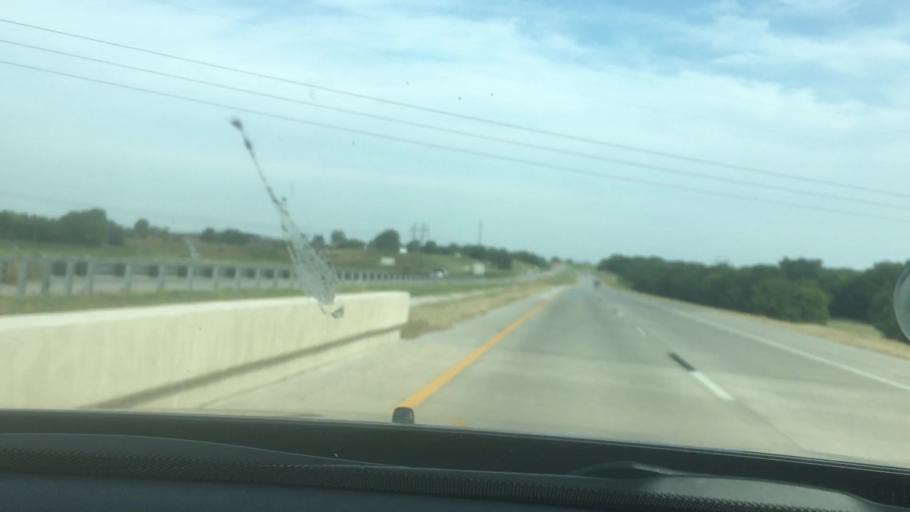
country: US
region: Oklahoma
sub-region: Pontotoc County
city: Ada
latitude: 34.7795
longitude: -96.7104
